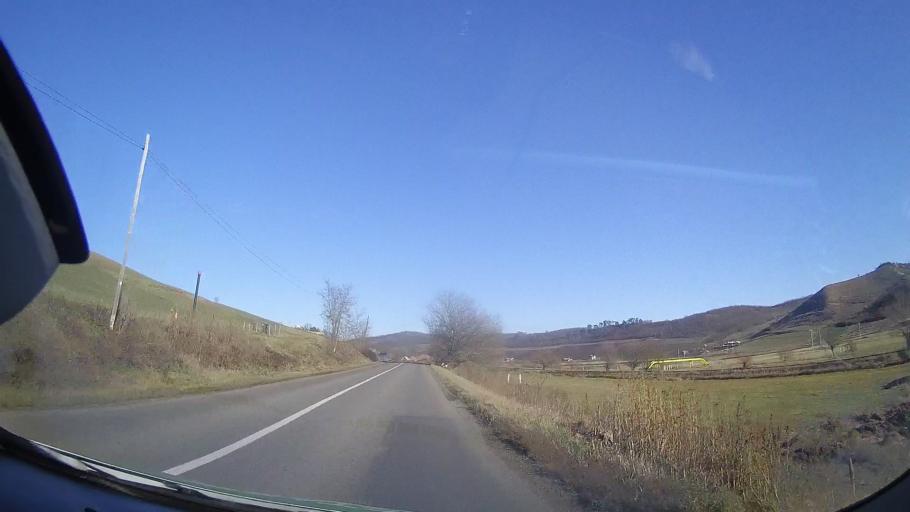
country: RO
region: Mures
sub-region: Comuna Sarmasu
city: Sarmasu
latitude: 46.7721
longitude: 24.1966
